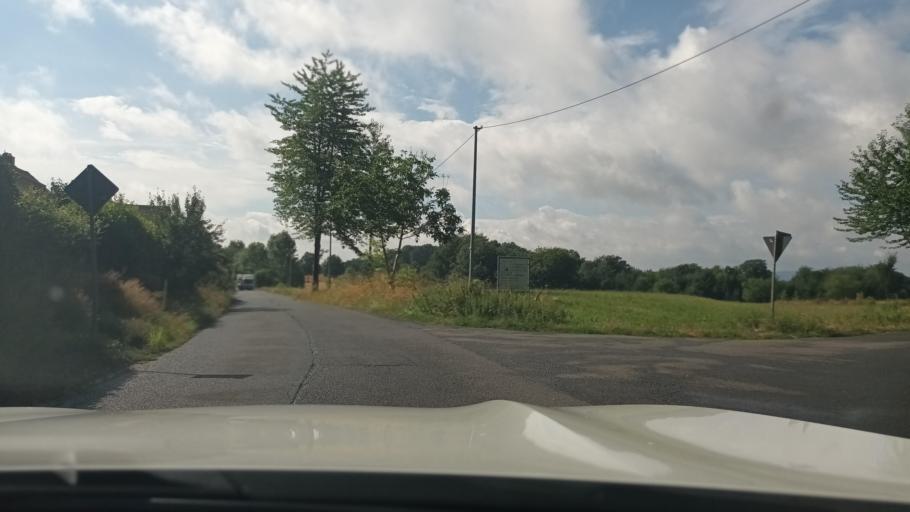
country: DE
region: North Rhine-Westphalia
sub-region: Regierungsbezirk Koln
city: Hennef
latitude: 50.7954
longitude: 7.3005
